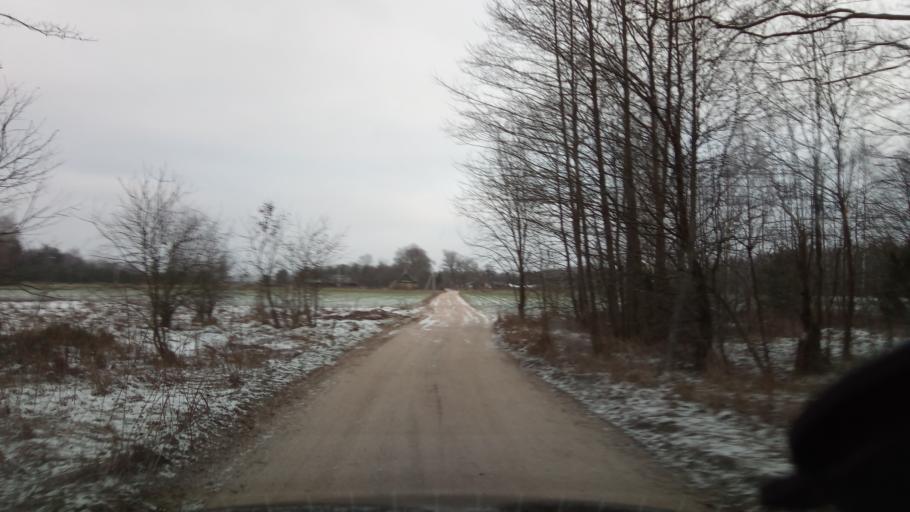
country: LT
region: Alytaus apskritis
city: Varena
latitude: 54.1242
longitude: 24.7056
